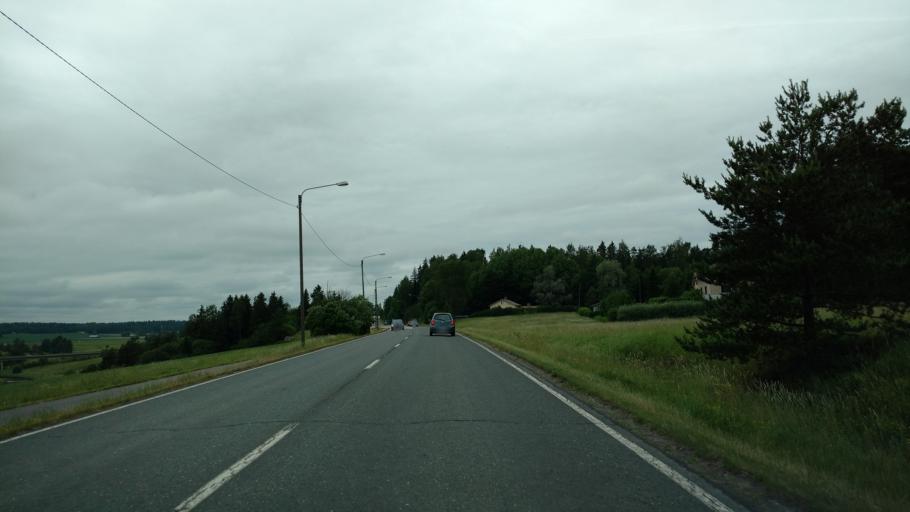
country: FI
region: Varsinais-Suomi
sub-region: Salo
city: Halikko
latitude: 60.4072
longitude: 23.0651
